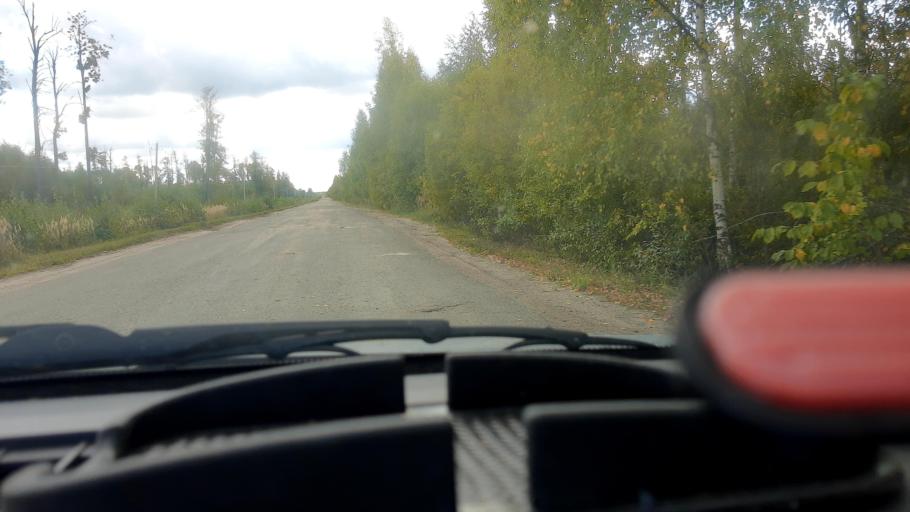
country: RU
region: Mariy-El
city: Kilemary
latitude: 56.8985
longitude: 46.7456
